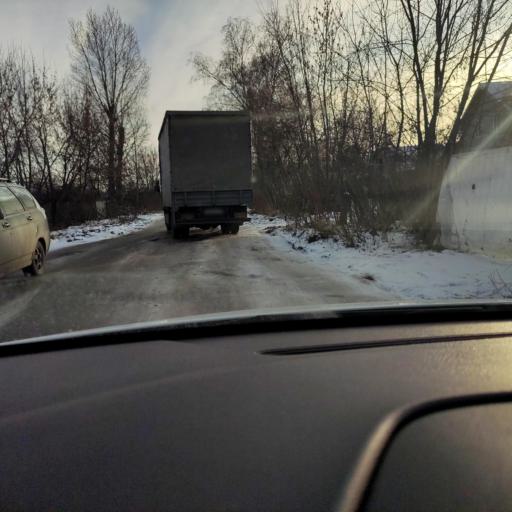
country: RU
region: Tatarstan
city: Staroye Arakchino
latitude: 55.8653
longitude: 49.0469
